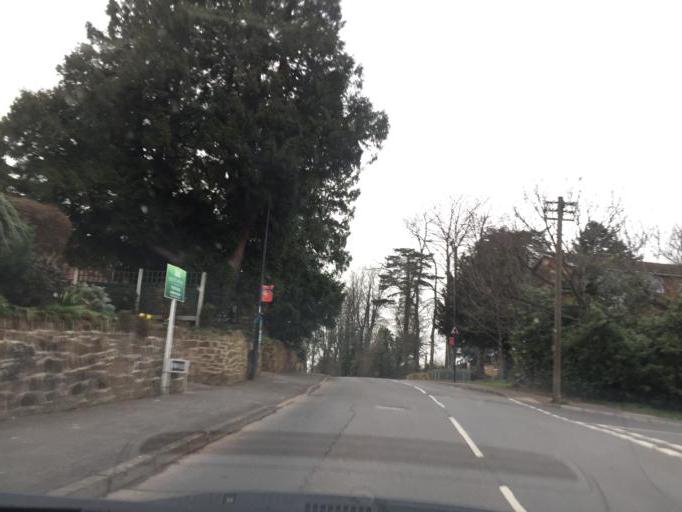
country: GB
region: England
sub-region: Warwickshire
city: Kenilworth
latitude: 52.3487
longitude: -1.5664
